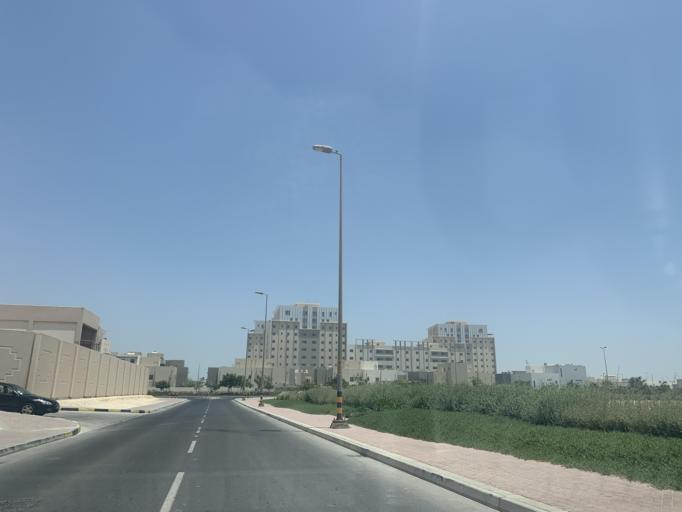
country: BH
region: Manama
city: Jidd Hafs
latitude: 26.2352
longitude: 50.4645
